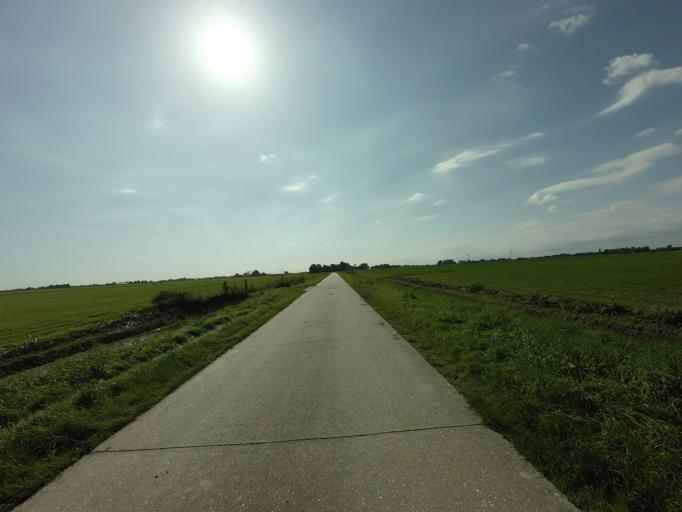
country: NL
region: Friesland
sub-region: Gemeente Littenseradiel
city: Makkum
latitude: 53.0972
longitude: 5.6481
